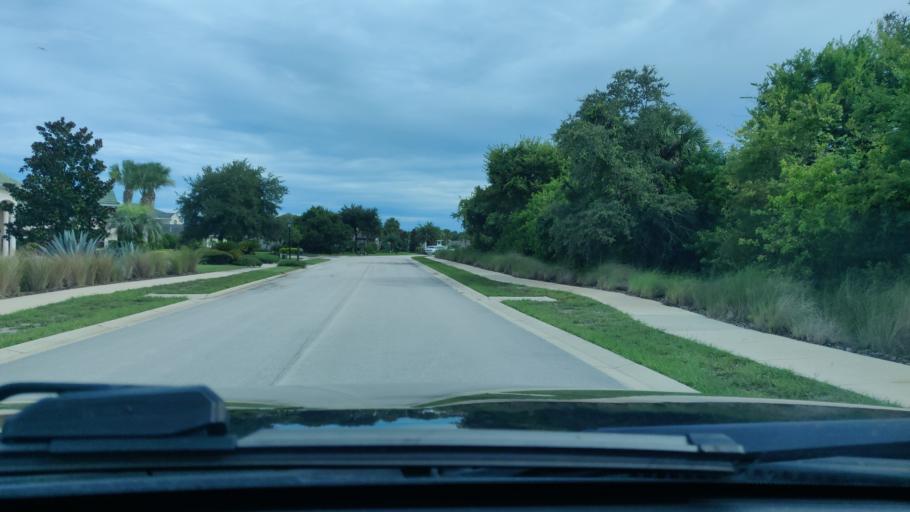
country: US
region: Florida
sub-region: Flagler County
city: Flagler Beach
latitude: 29.5167
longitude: -81.1587
